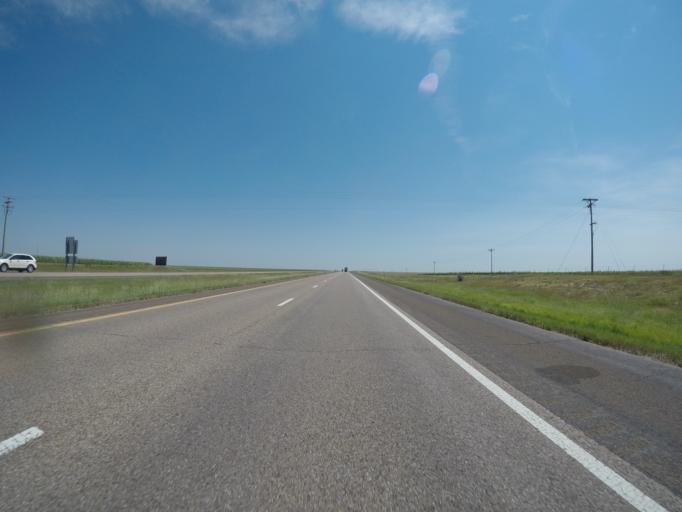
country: US
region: Kansas
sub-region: Thomas County
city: Colby
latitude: 39.3479
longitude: -101.3543
